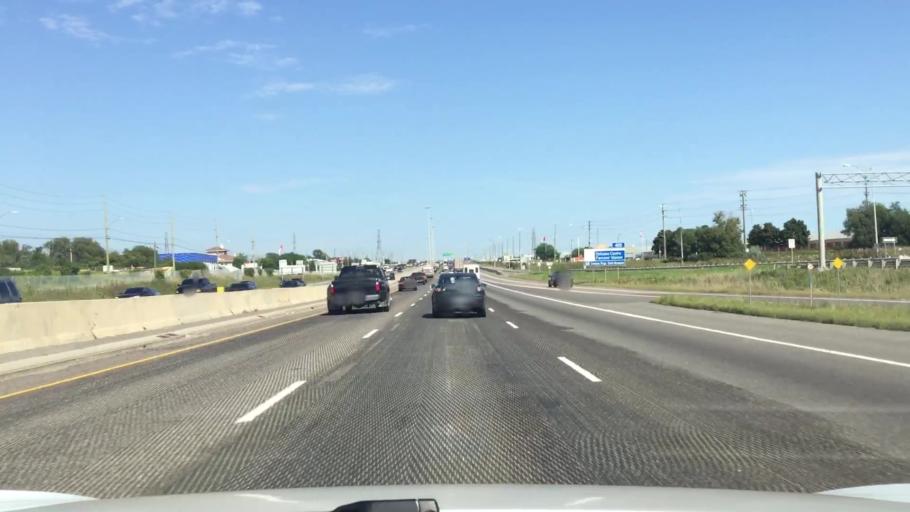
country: CA
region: Ontario
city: Oshawa
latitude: 43.8691
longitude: -78.8964
